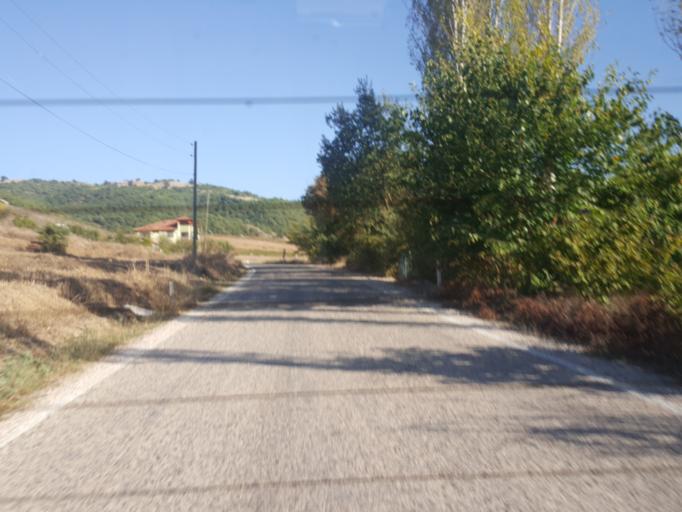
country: TR
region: Amasya
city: Tasova
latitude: 40.7319
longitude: 36.2861
